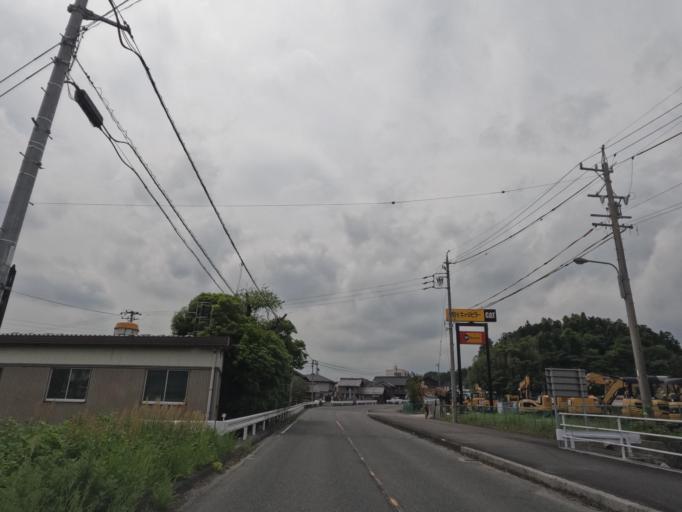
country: JP
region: Mie
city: Komono
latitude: 35.1431
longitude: 136.5184
